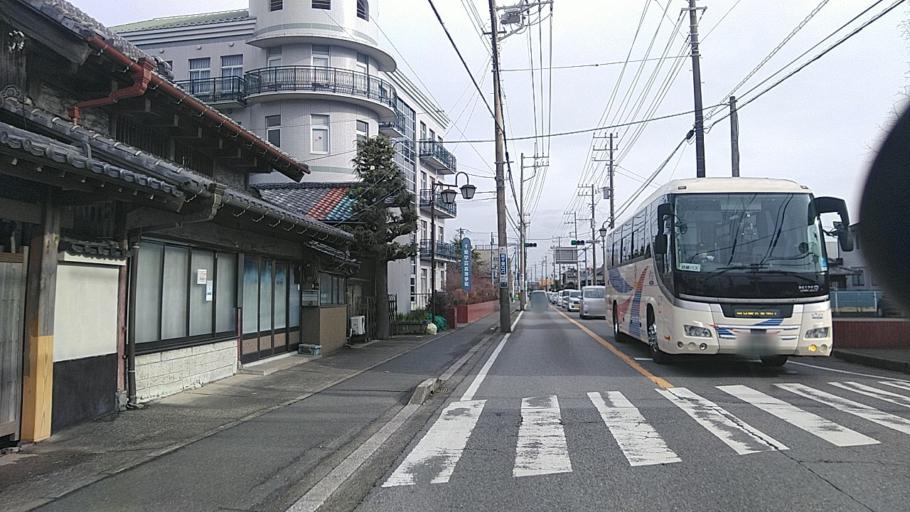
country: JP
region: Chiba
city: Togane
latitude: 35.5737
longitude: 140.3723
